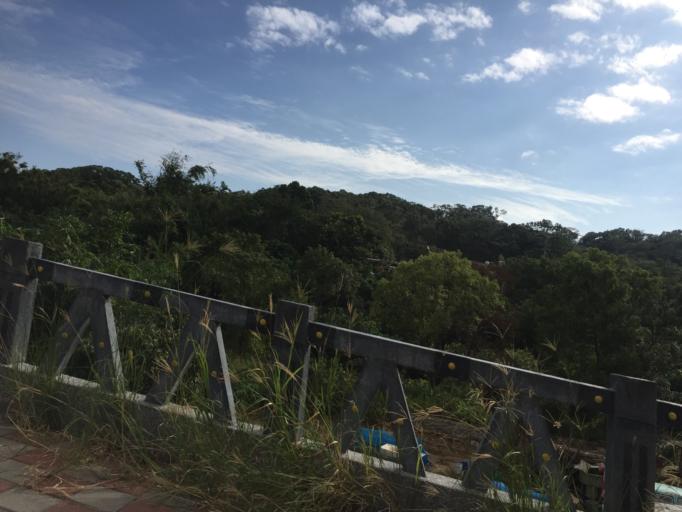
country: TW
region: Taiwan
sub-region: Hsinchu
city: Hsinchu
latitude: 24.7736
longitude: 120.9503
